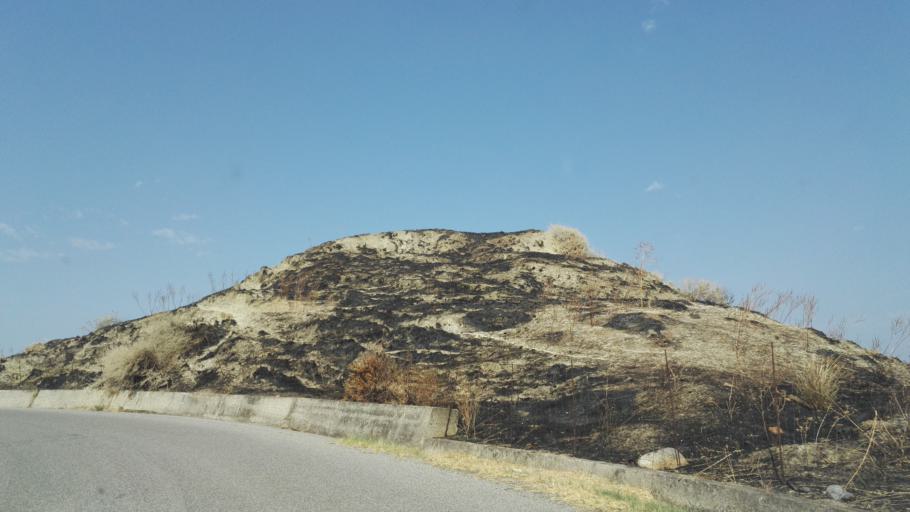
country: IT
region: Calabria
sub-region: Provincia di Reggio Calabria
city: Monasterace
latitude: 38.4493
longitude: 16.5411
